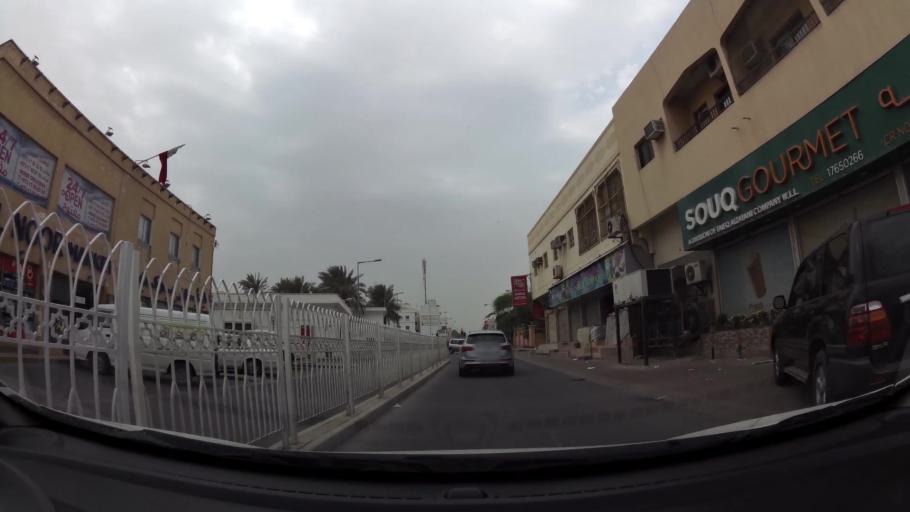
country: BH
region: Northern
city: Ar Rifa'
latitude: 26.1277
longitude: 50.5421
